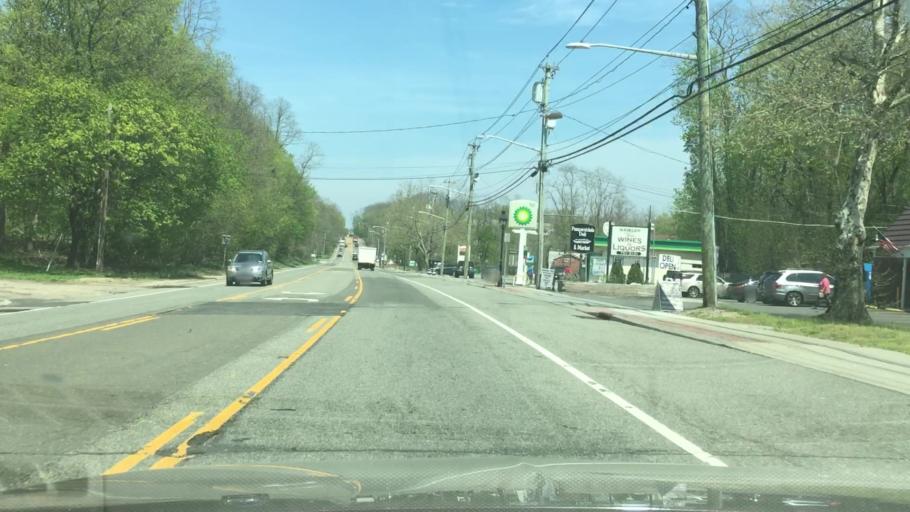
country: US
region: New York
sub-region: Suffolk County
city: Setauket-East Setauket
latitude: 40.9277
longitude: -73.1178
